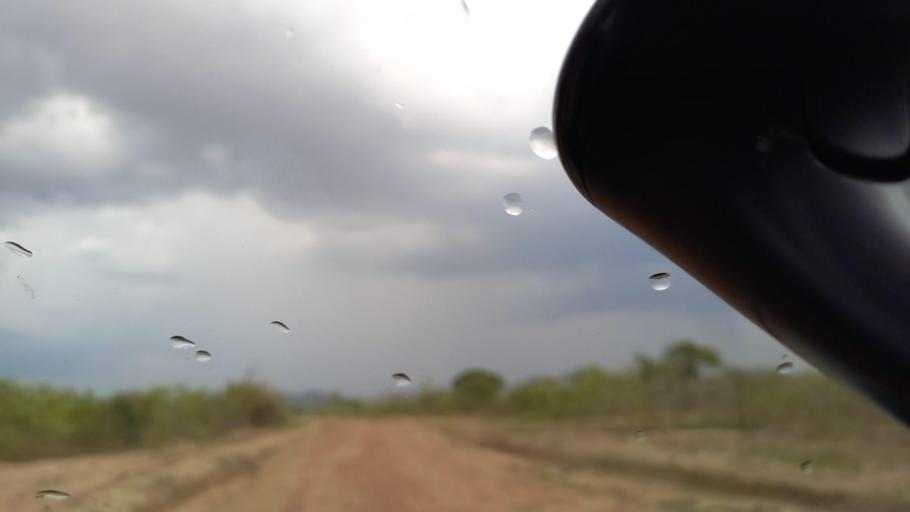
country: ZM
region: Lusaka
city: Kafue
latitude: -15.8530
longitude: 28.1129
